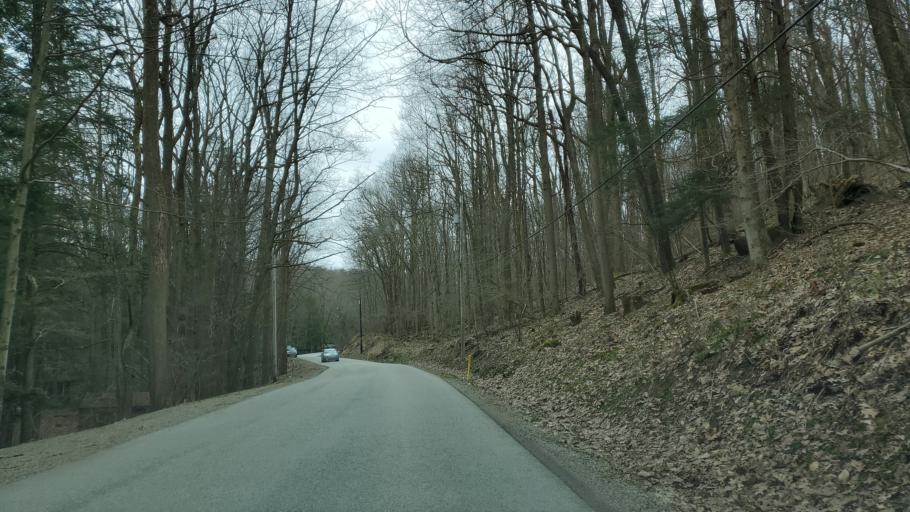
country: US
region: Pennsylvania
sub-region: Westmoreland County
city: Ligonier
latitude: 40.1710
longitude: -79.2357
